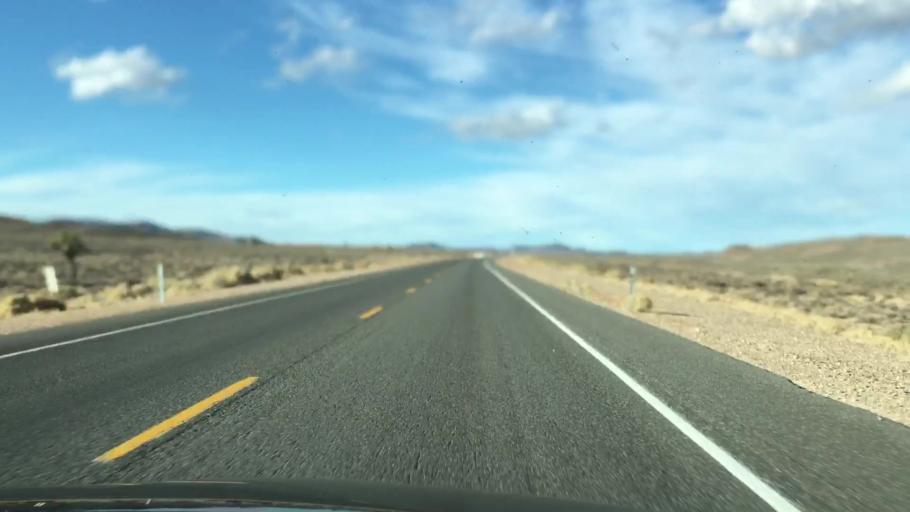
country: US
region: Nevada
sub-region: Esmeralda County
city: Goldfield
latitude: 37.5398
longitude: -117.1949
